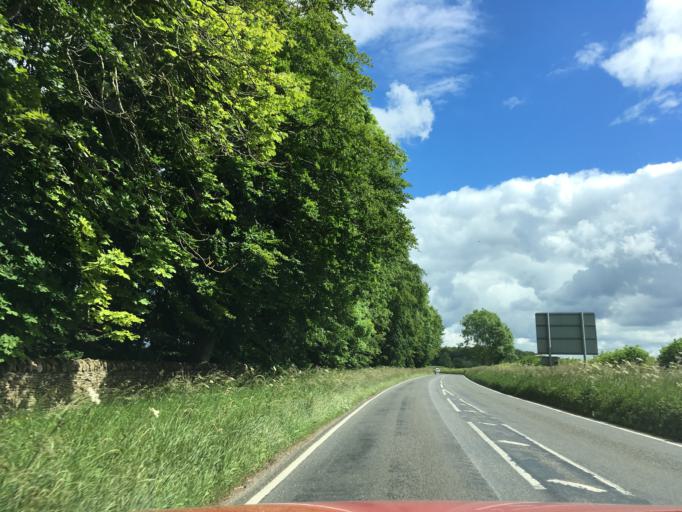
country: GB
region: England
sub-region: Oxfordshire
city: Chipping Norton
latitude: 51.9092
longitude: -1.5547
